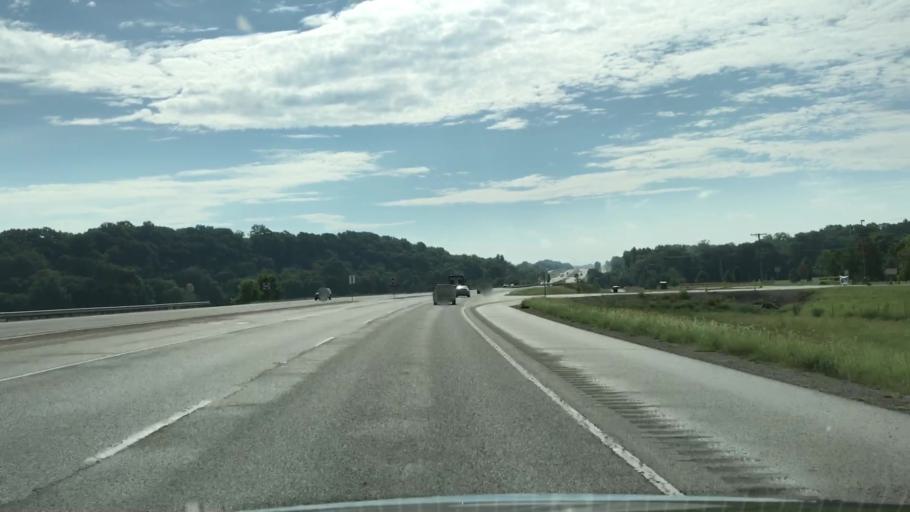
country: US
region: Kentucky
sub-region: Warren County
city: Plano
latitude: 36.8996
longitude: -86.3867
